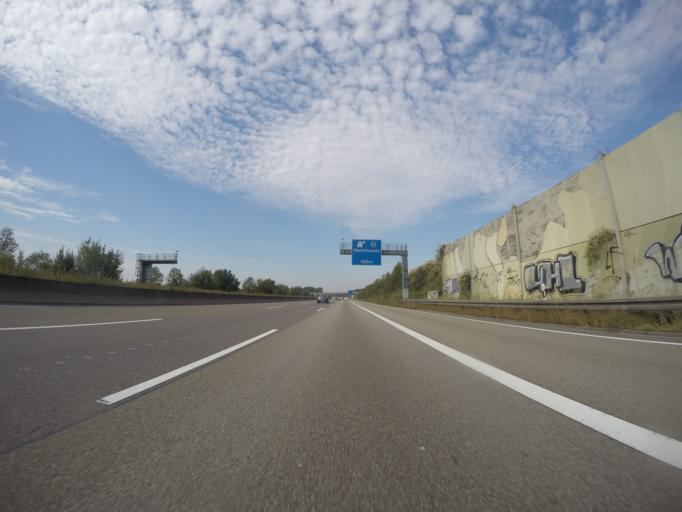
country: DE
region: Hesse
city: Obertshausen
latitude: 50.0647
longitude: 8.8376
